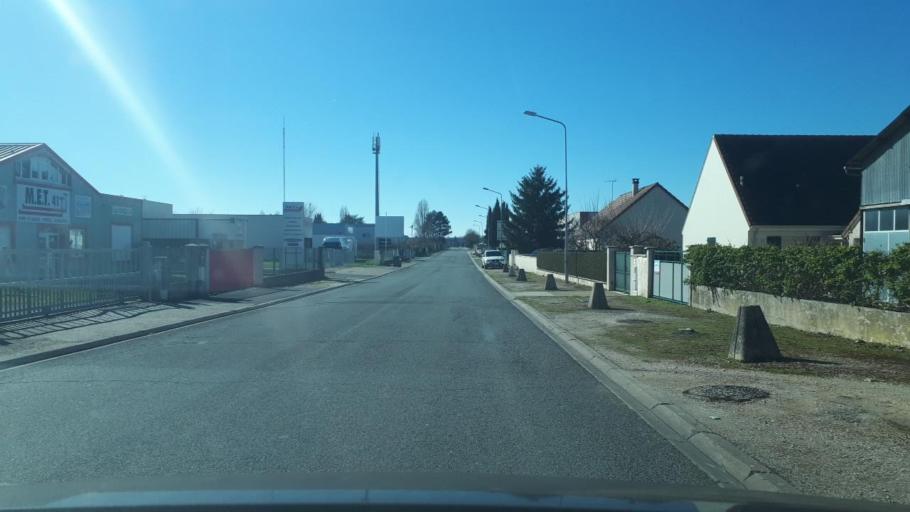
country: FR
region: Centre
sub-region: Departement du Loir-et-Cher
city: Vineuil
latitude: 47.5693
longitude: 1.3791
